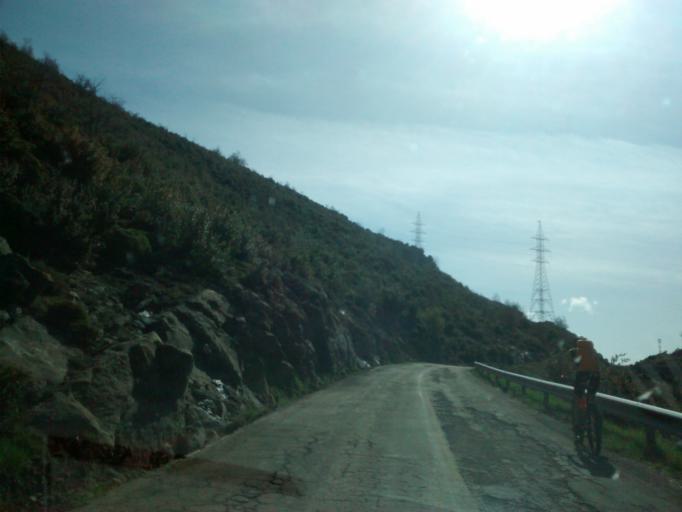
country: ES
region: Aragon
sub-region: Provincia de Huesca
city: Arguis
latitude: 42.3272
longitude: -0.4169
